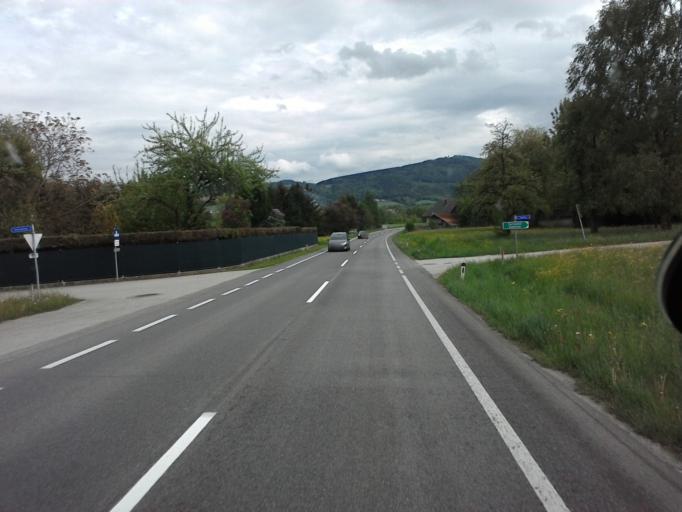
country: AT
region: Upper Austria
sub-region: Politischer Bezirk Kirchdorf an der Krems
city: Micheldorf in Oberoesterreich
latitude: 47.9500
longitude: 14.0954
